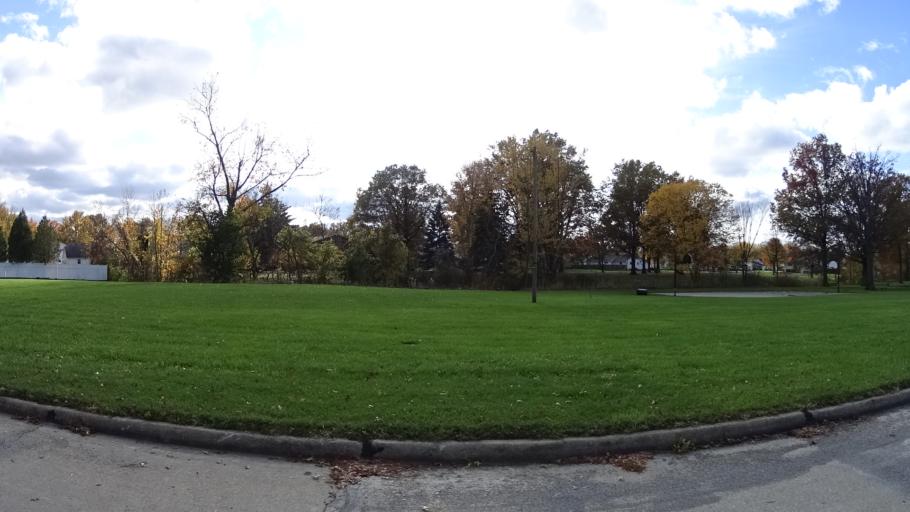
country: US
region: Ohio
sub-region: Lorain County
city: Lorain
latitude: 41.4397
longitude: -82.1921
